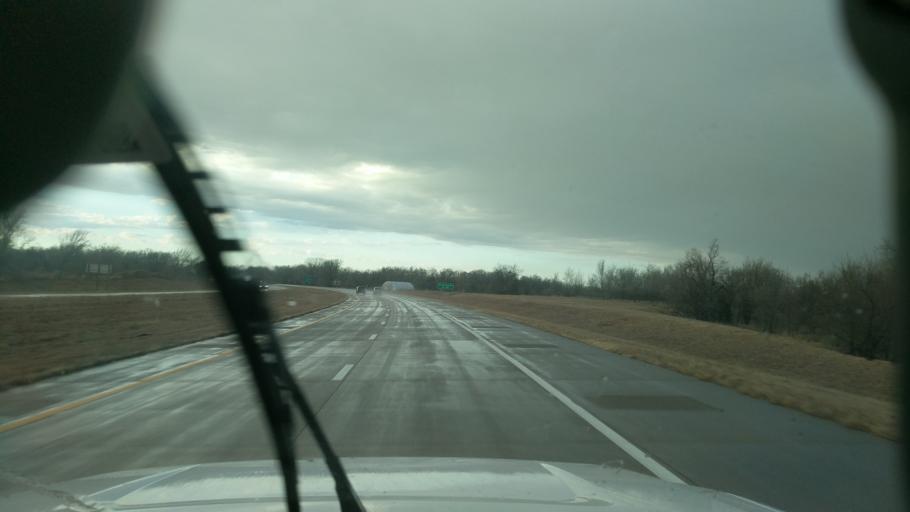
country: US
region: Kansas
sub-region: Harvey County
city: North Newton
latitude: 38.0773
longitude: -97.3312
